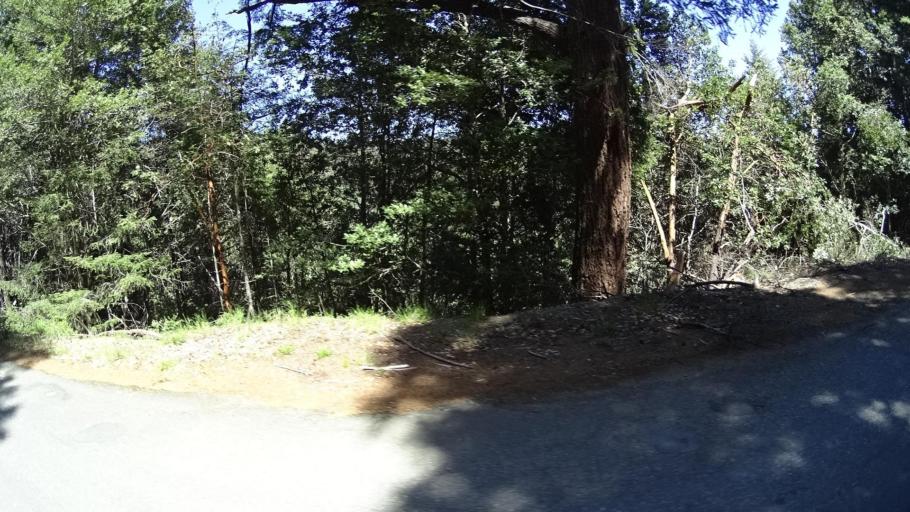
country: US
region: California
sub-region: Humboldt County
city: Rio Dell
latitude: 40.2690
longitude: -124.0775
